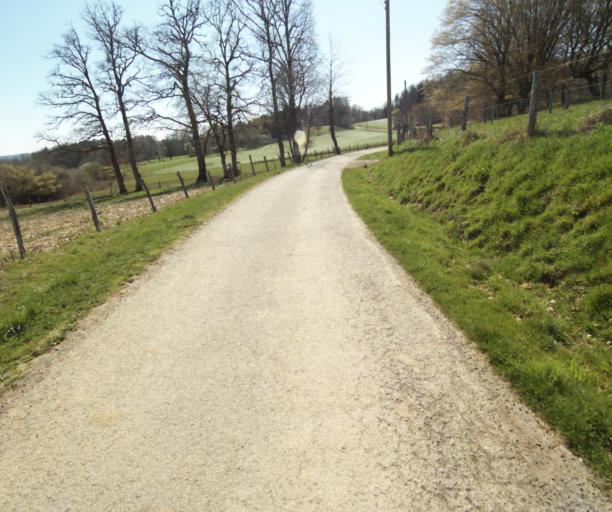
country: FR
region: Limousin
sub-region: Departement de la Correze
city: Chameyrat
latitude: 45.2496
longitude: 1.7056
